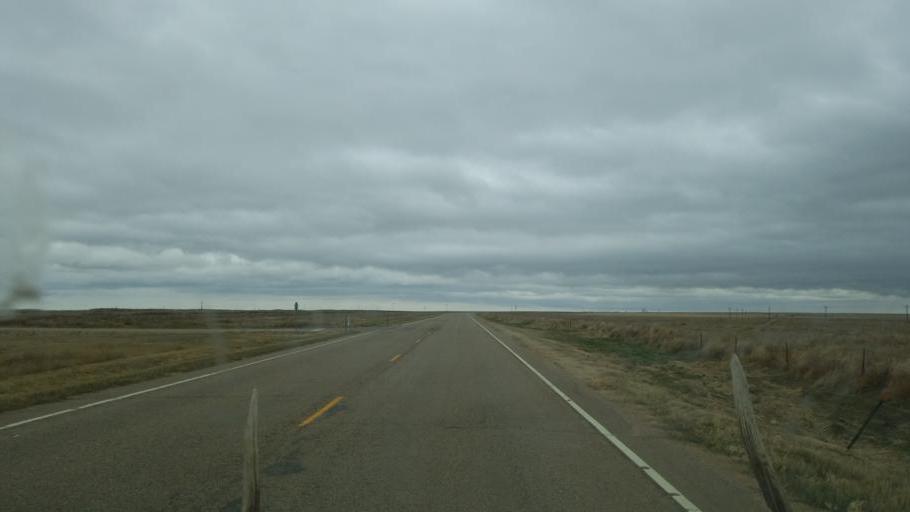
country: US
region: Colorado
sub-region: Cheyenne County
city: Cheyenne Wells
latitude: 38.8090
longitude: -102.5925
